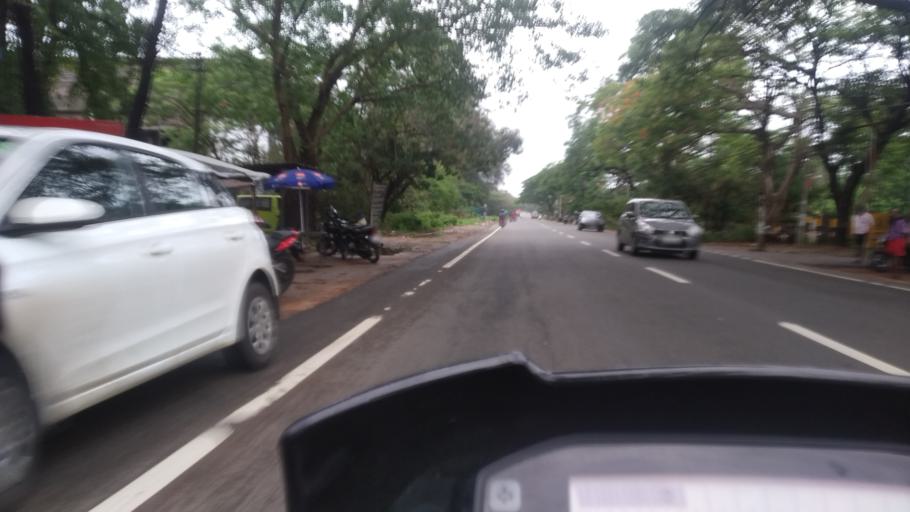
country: IN
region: Kerala
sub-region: Alappuzha
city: Alleppey
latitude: 9.5490
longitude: 76.3274
